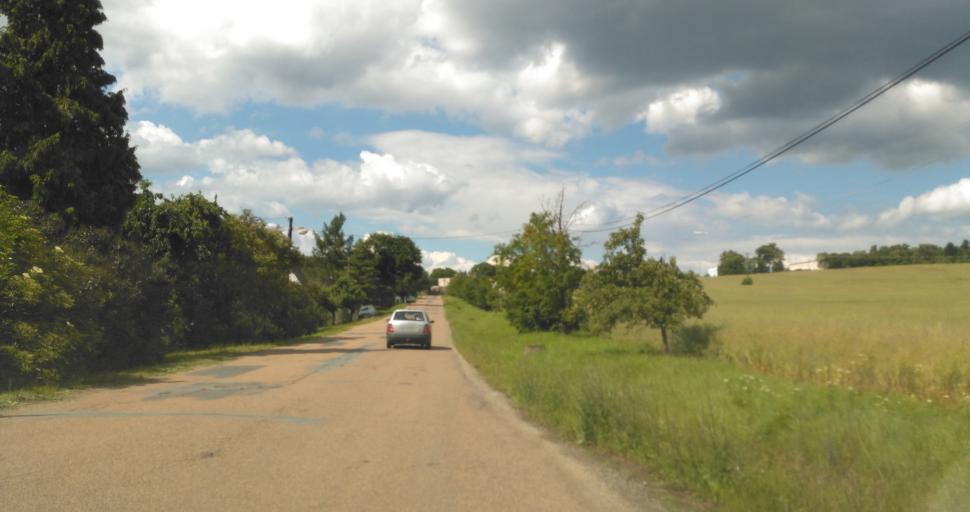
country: CZ
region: Plzensky
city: Zbiroh
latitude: 49.8528
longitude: 13.7525
